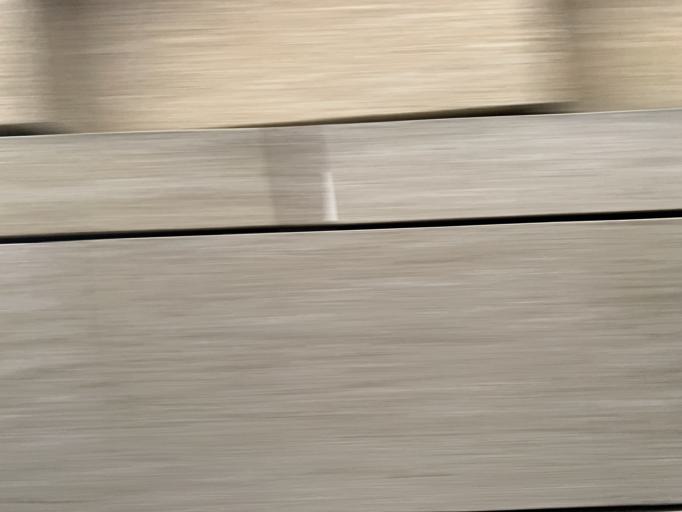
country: FR
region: Rhone-Alpes
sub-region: Departement du Rhone
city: Meyzieu
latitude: 45.7726
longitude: 4.9907
